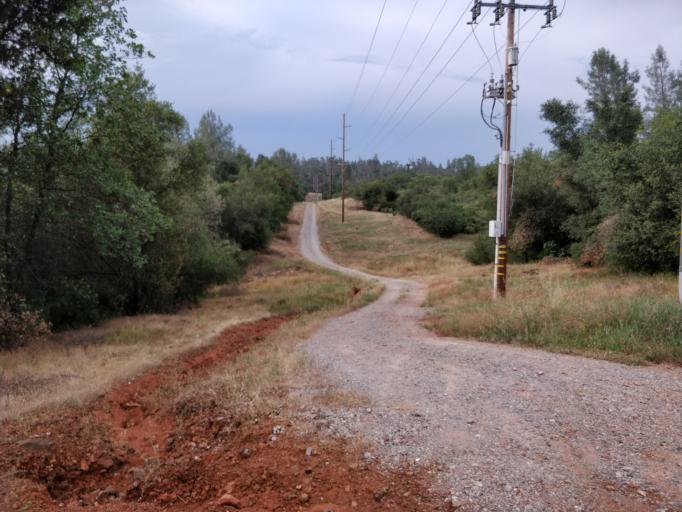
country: US
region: California
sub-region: Shasta County
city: Central Valley (historical)
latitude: 40.6617
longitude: -122.3751
